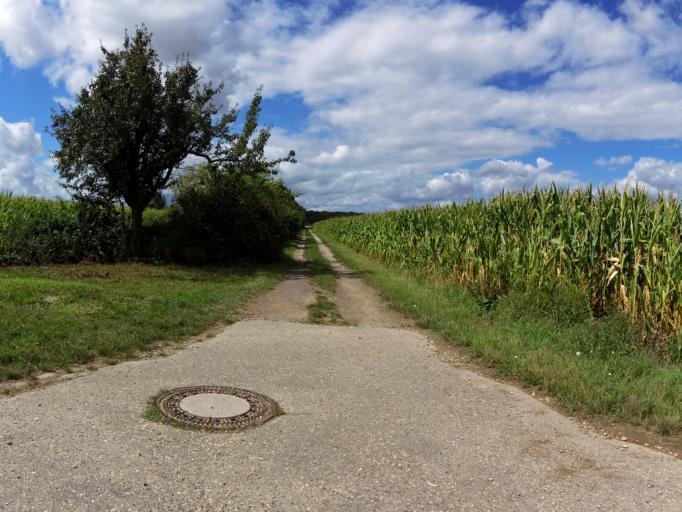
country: DE
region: Baden-Wuerttemberg
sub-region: Freiburg Region
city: Lahr
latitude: 48.3697
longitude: 7.8352
